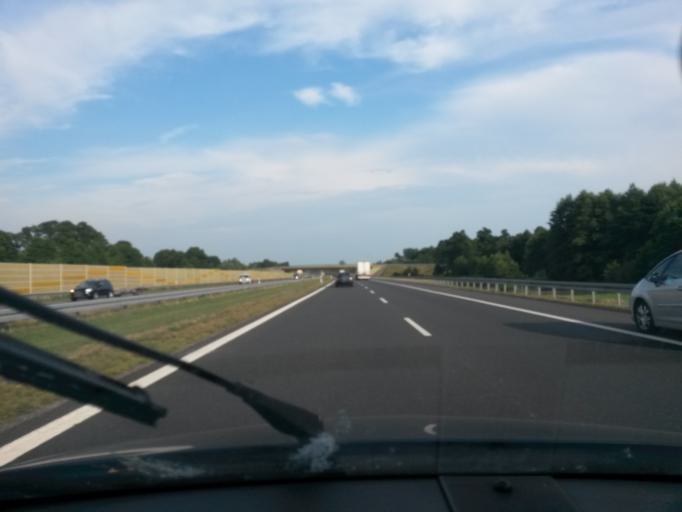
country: PL
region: Lodz Voivodeship
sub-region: Powiat poddebicki
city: Wartkowice
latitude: 51.9750
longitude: 19.0823
